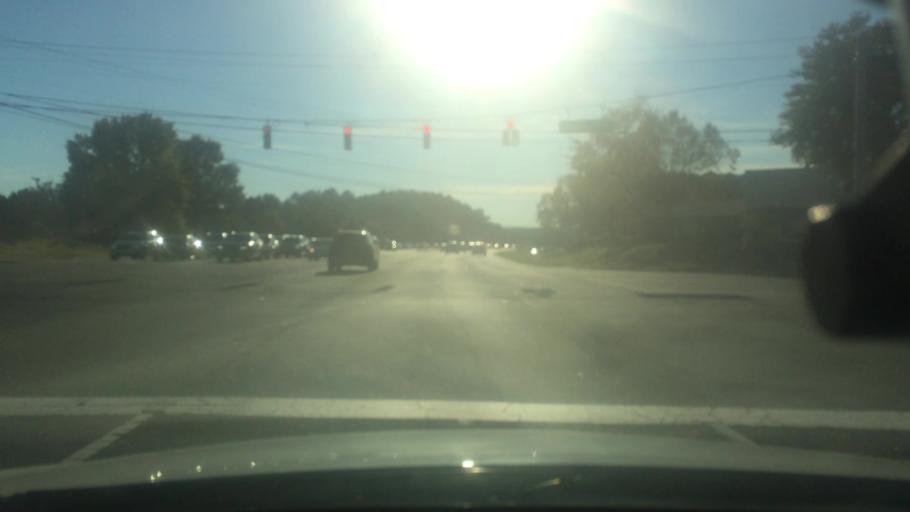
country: US
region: North Carolina
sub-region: Orange County
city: Chapel Hill
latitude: 35.9119
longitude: -78.9840
